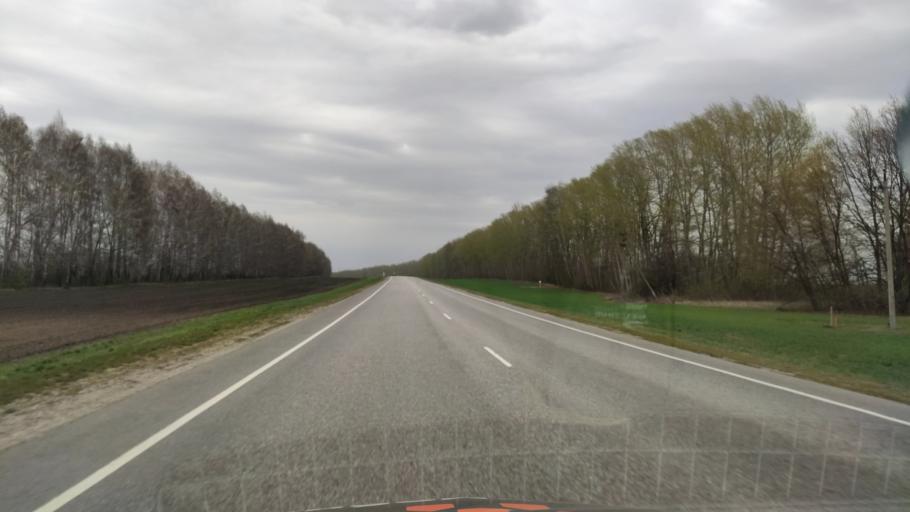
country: RU
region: Kursk
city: Olym
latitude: 51.5503
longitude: 38.1917
